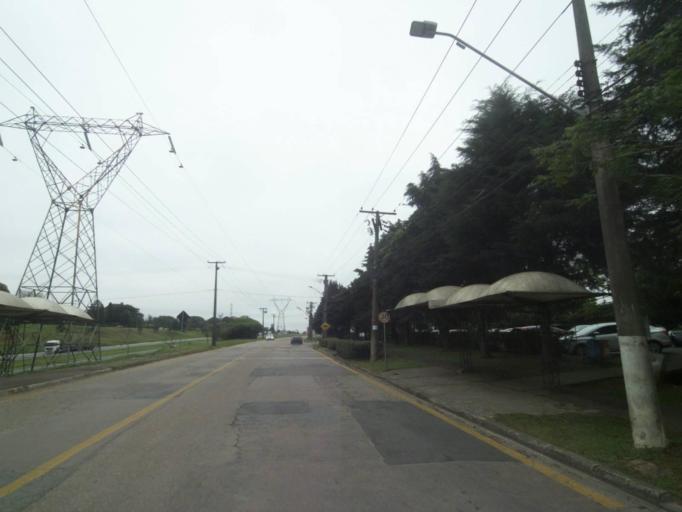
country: BR
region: Parana
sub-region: Araucaria
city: Araucaria
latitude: -25.5456
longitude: -49.3177
